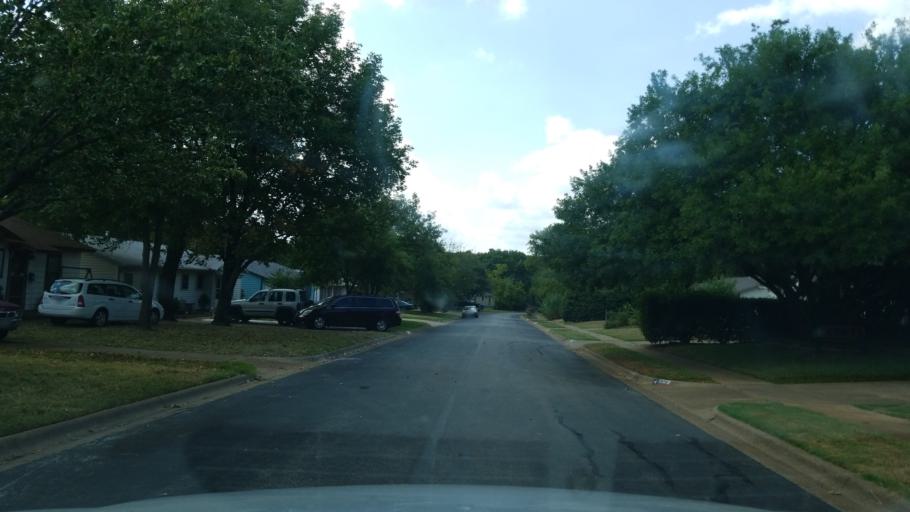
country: US
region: Texas
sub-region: Tarrant County
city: Euless
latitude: 32.8482
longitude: -97.0871
